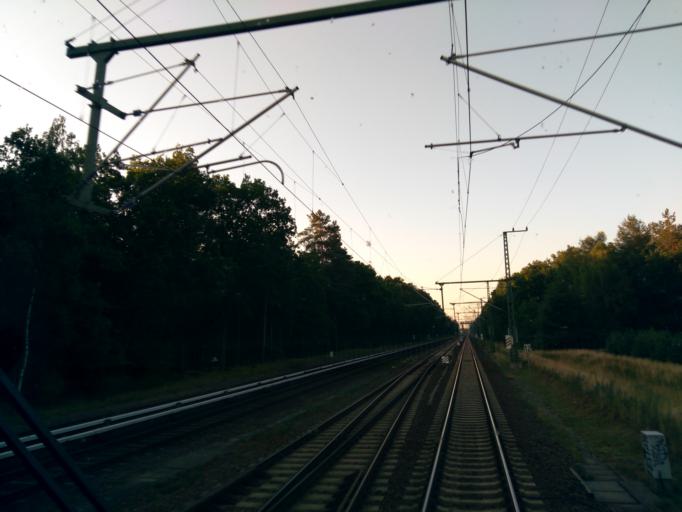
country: DE
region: Brandenburg
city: Zeuthen
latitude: 52.3873
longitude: 13.6047
